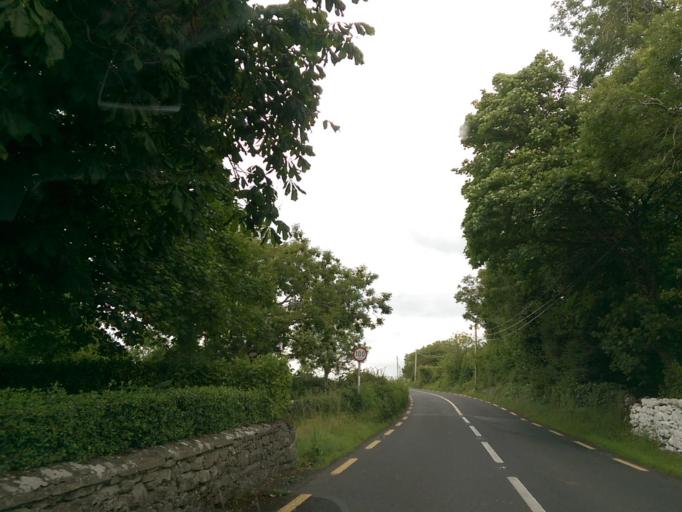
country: IE
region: Connaught
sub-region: County Galway
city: Bearna
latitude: 53.1279
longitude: -9.1225
